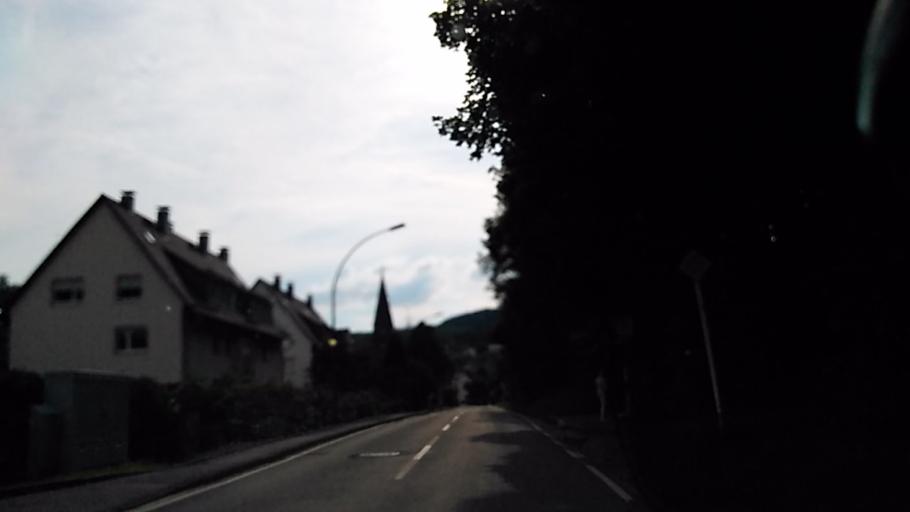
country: DE
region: North Rhine-Westphalia
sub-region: Regierungsbezirk Arnsberg
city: Herscheid
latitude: 51.2234
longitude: 7.7010
